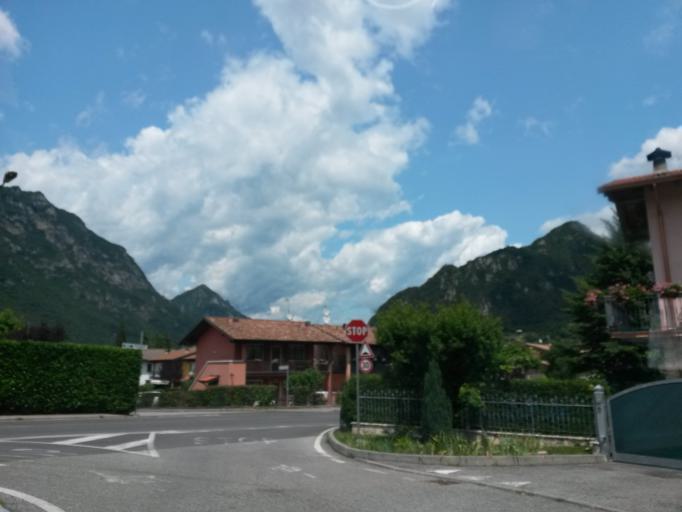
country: IT
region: Lombardy
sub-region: Provincia di Brescia
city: Crone
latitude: 45.7384
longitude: 10.4774
